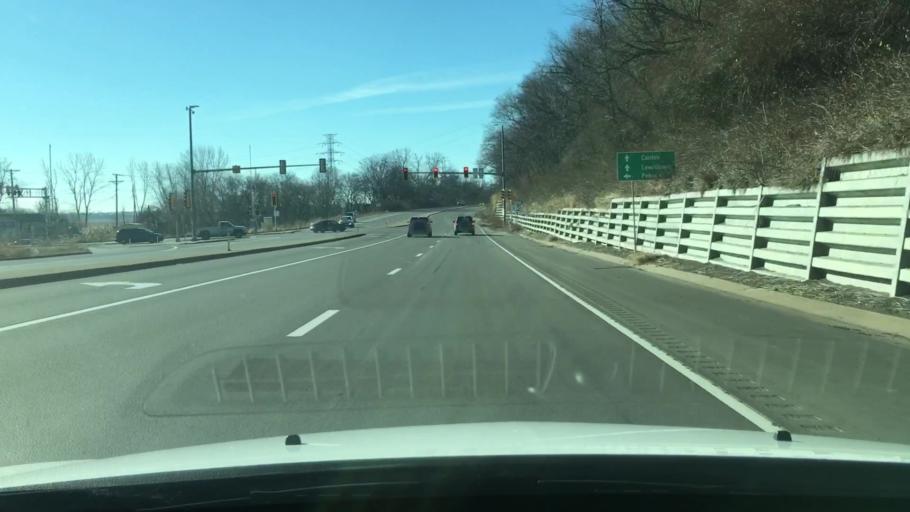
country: US
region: Illinois
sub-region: Tazewell County
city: Pekin
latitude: 40.5902
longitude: -89.6777
